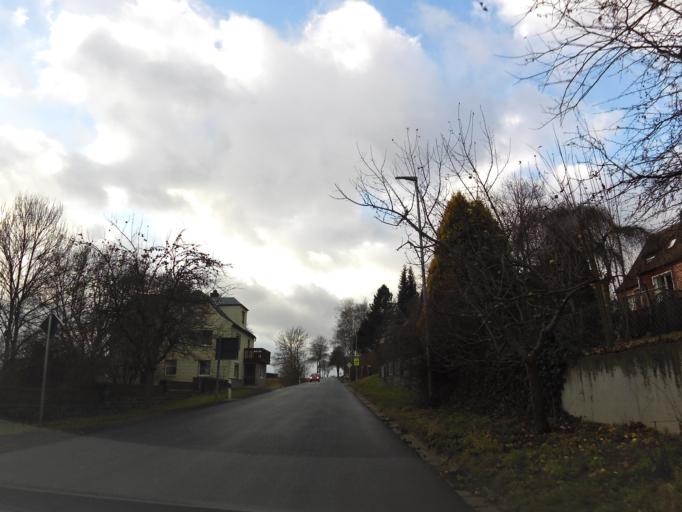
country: DE
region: Bavaria
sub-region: Upper Franconia
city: Hochstadt bei Thiersheim
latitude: 50.0728
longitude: 12.0524
